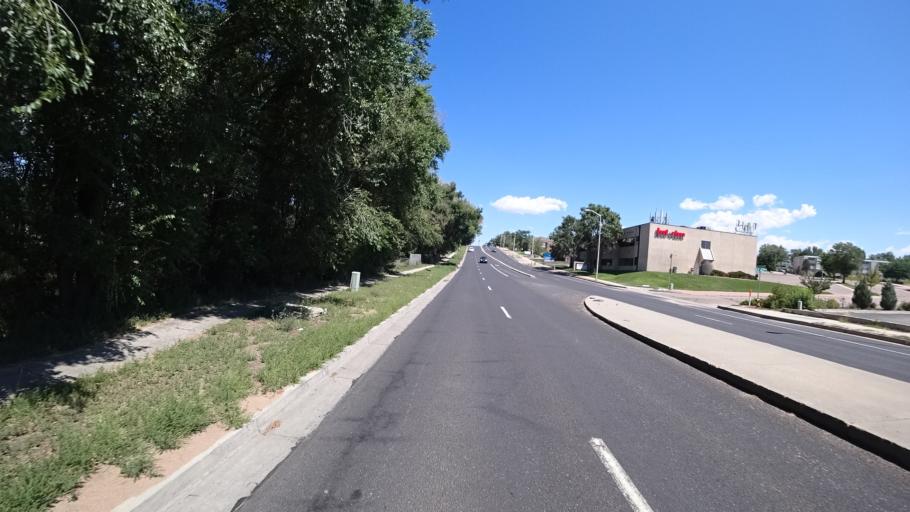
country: US
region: Colorado
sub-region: El Paso County
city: Colorado Springs
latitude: 38.8591
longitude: -104.7943
